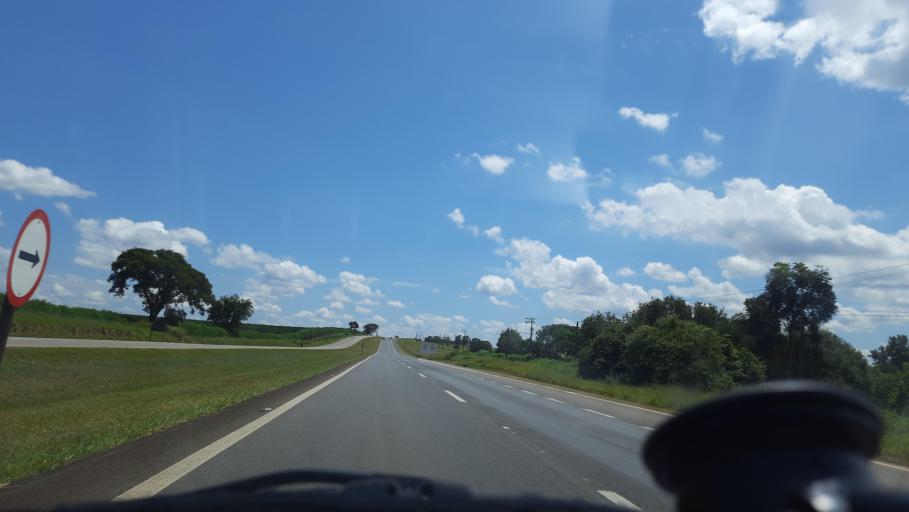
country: BR
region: Sao Paulo
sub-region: Moji-Guacu
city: Mogi-Gaucu
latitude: -22.2629
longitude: -46.9753
